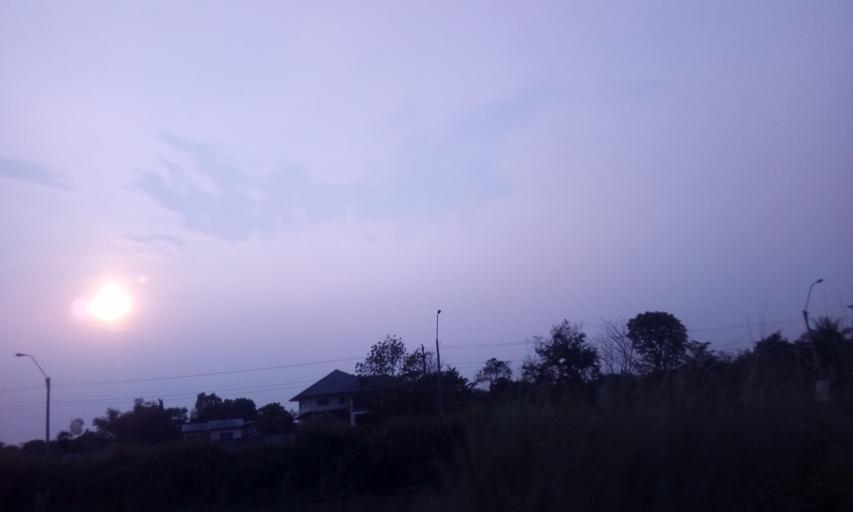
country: TH
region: Bangkok
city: Nong Chok
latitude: 13.8703
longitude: 100.8796
